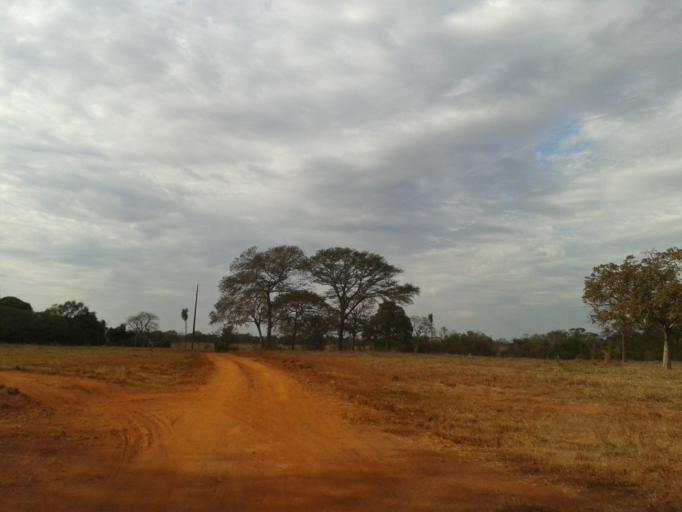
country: BR
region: Minas Gerais
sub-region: Santa Vitoria
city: Santa Vitoria
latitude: -18.7432
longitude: -50.2121
